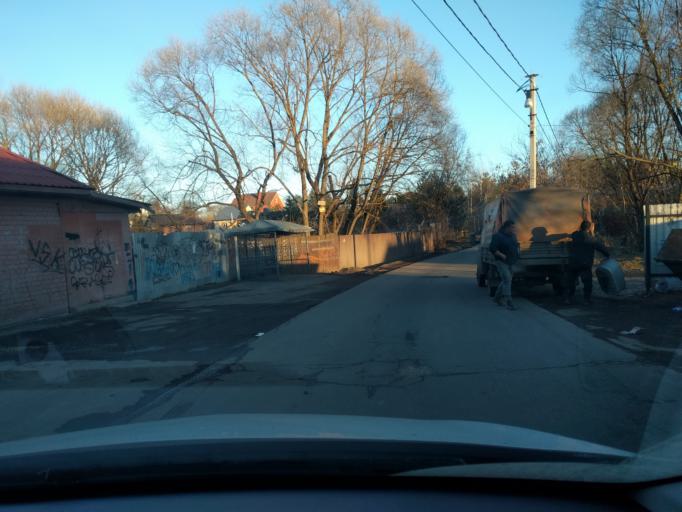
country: RU
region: Moskovskaya
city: Dubrovitsy
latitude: 55.4919
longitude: 37.4295
